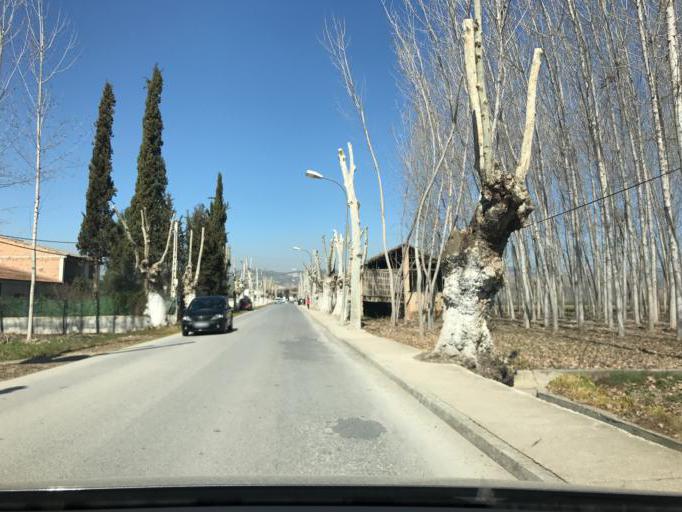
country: ES
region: Andalusia
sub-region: Provincia de Granada
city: Fuente Vaqueros
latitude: 37.2293
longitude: -3.7889
